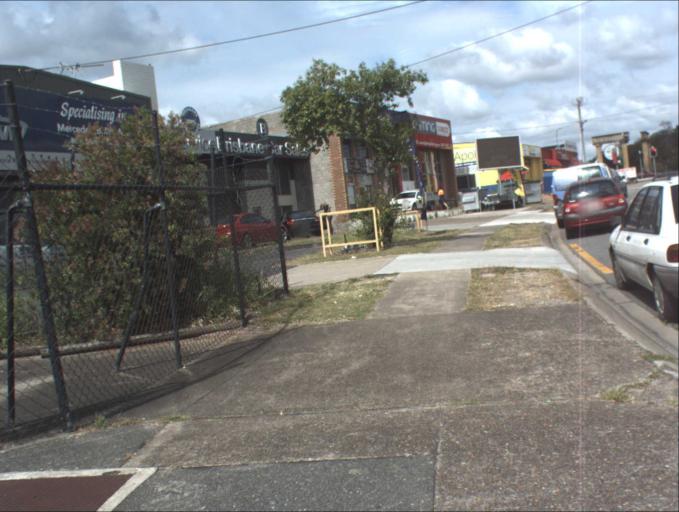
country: AU
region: Queensland
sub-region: Logan
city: Springwood
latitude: -27.6117
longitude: 153.1140
